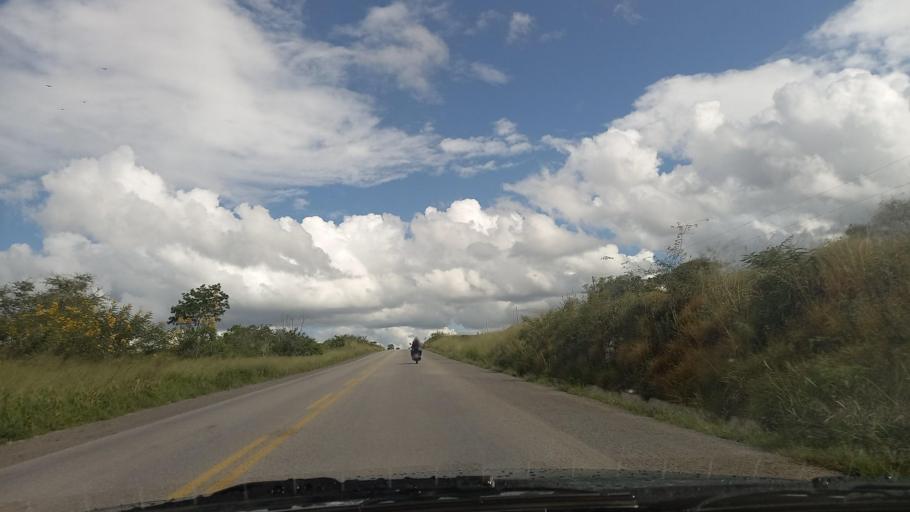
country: BR
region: Pernambuco
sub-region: Lajedo
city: Lajedo
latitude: -8.5869
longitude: -36.2892
